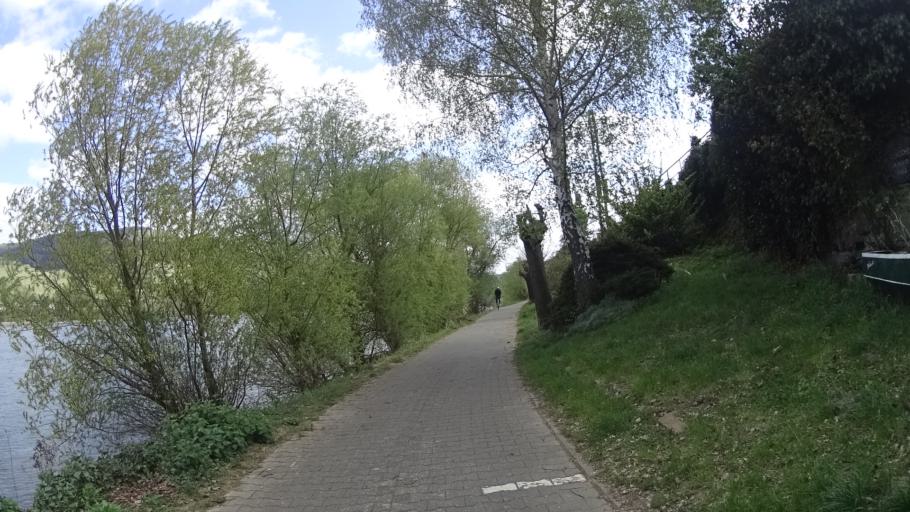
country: DE
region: Rheinland-Pfalz
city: Niederheimbach
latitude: 50.0318
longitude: 7.8115
